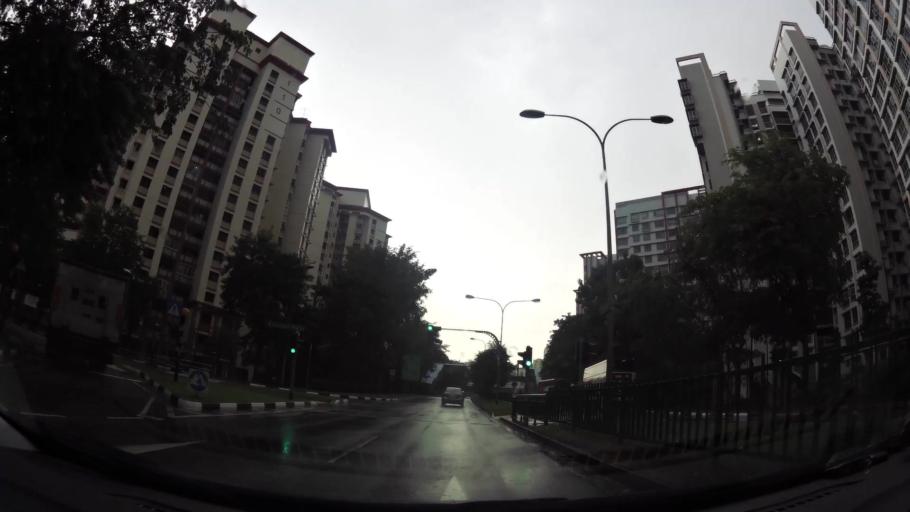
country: MY
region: Johor
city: Kampung Pasir Gudang Baru
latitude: 1.3843
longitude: 103.9001
